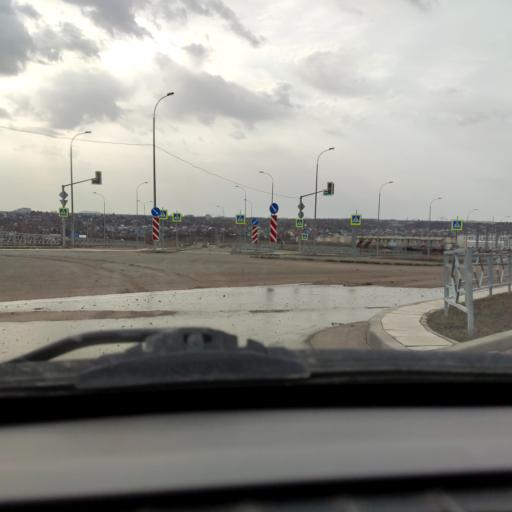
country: RU
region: Samara
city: Petra-Dubrava
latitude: 53.2920
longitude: 50.3331
